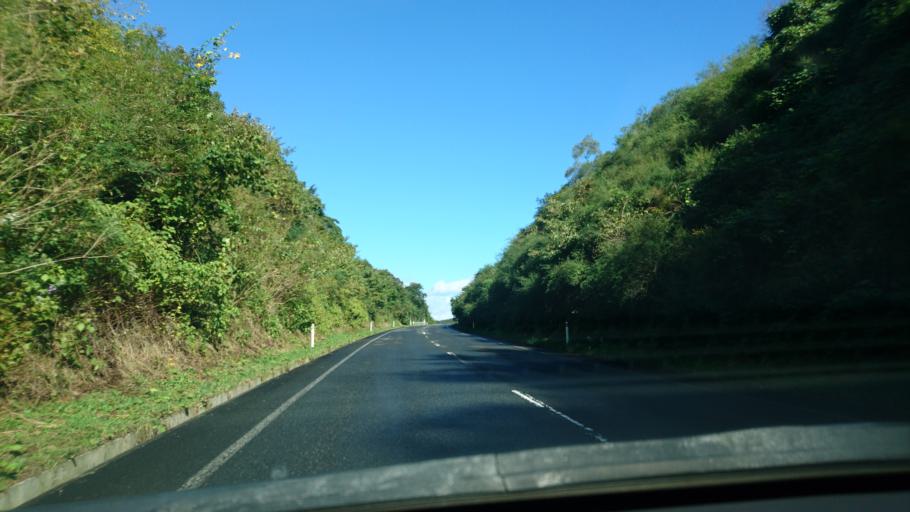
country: JP
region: Iwate
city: Ichinoseki
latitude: 39.0154
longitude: 141.0250
